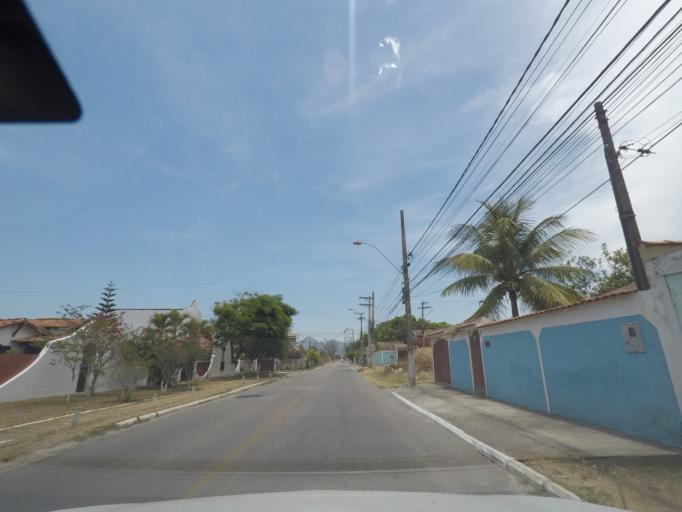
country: BR
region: Rio de Janeiro
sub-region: Marica
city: Marica
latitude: -22.9671
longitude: -42.9526
